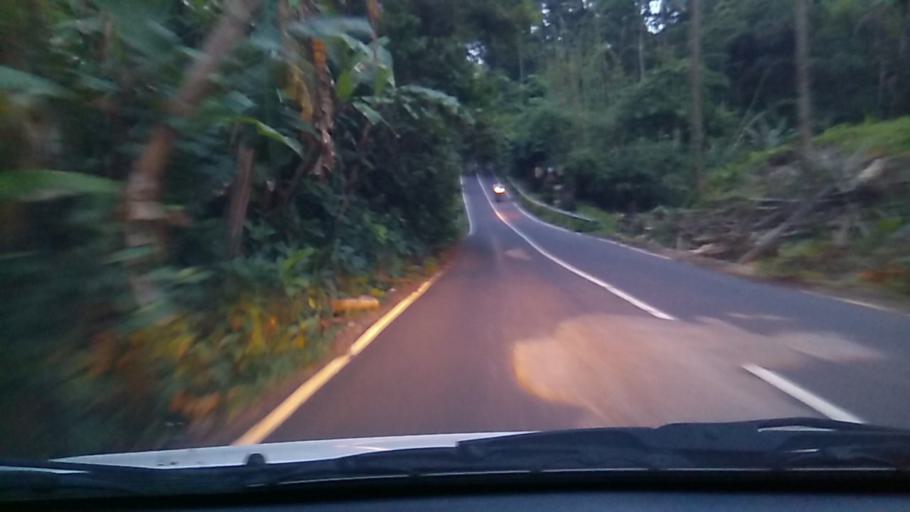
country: ID
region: Bali
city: Brahmana
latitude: -8.4734
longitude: 115.1989
